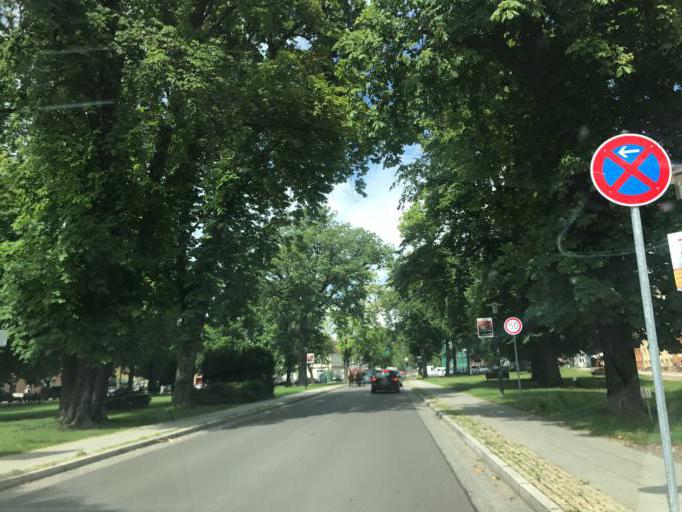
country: DE
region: Brandenburg
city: Rheinsberg
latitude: 53.0992
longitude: 12.8913
